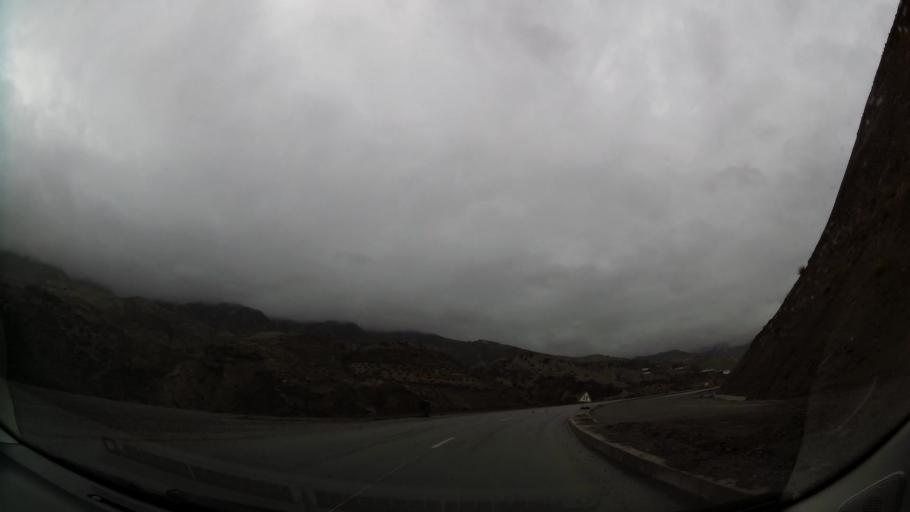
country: MA
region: Taza-Al Hoceima-Taounate
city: Imzourene
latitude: 35.0079
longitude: -3.8125
